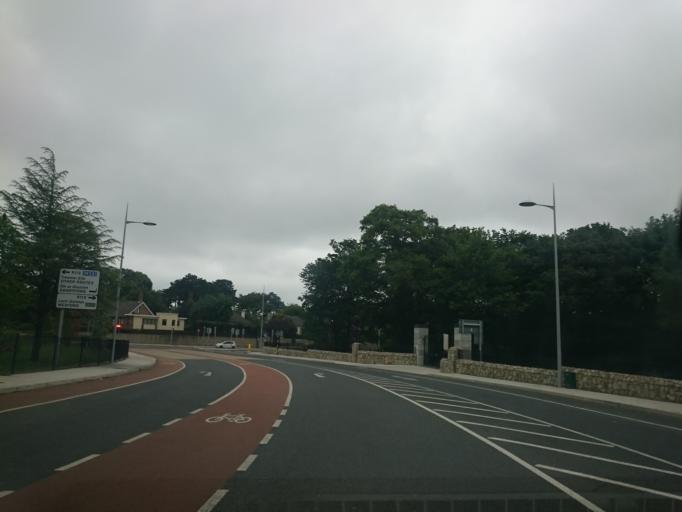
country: IE
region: Leinster
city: Foxrock
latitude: 53.2723
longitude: -6.1985
